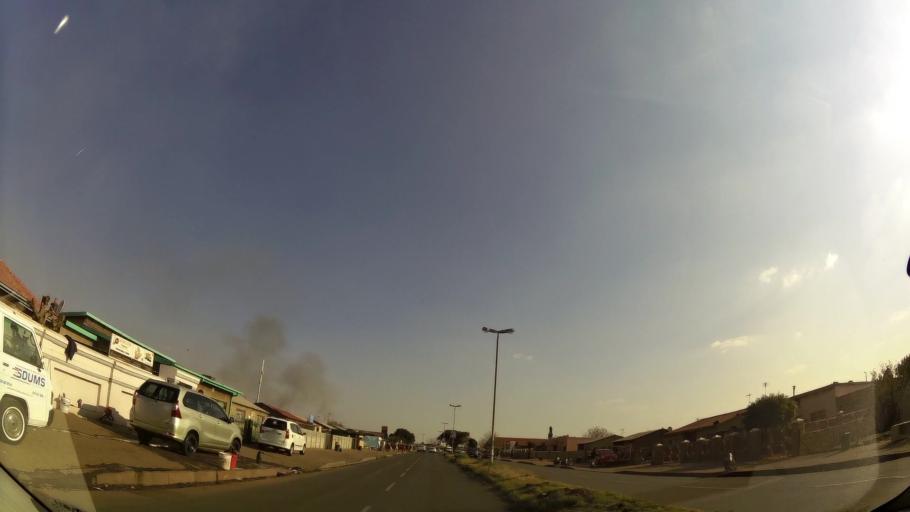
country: ZA
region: Gauteng
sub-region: Ekurhuleni Metropolitan Municipality
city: Brakpan
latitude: -26.1469
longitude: 28.4195
